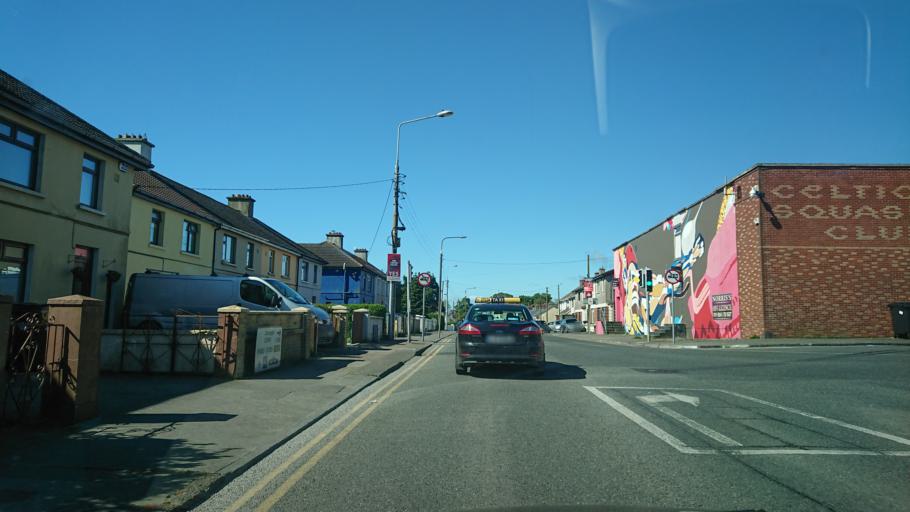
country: IE
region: Munster
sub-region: Waterford
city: Waterford
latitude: 52.2554
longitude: -7.1207
